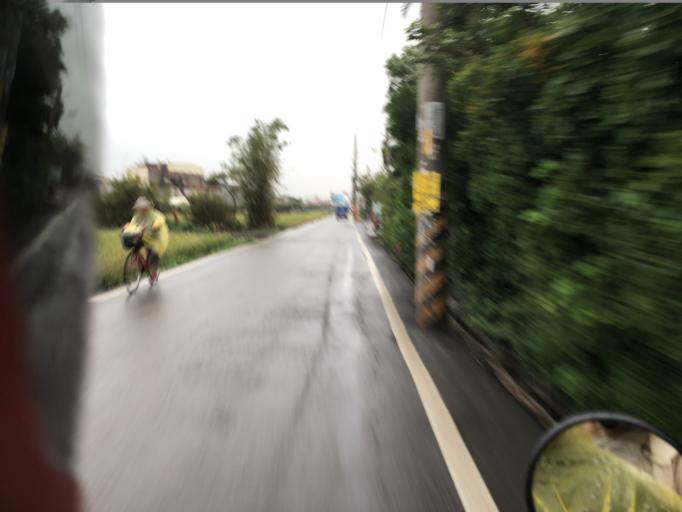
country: TW
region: Taiwan
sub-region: Hsinchu
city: Zhubei
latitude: 24.8454
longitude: 120.9871
